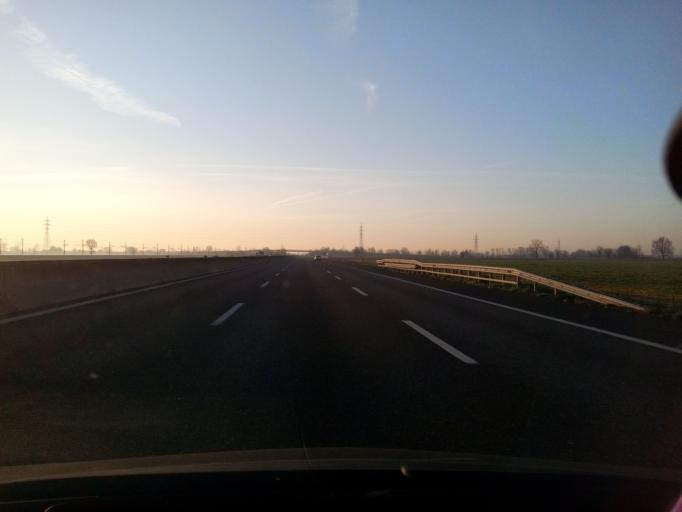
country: IT
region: Lombardy
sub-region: Provincia di Lodi
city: Salerano sul Lambro
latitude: 45.3134
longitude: 9.3882
